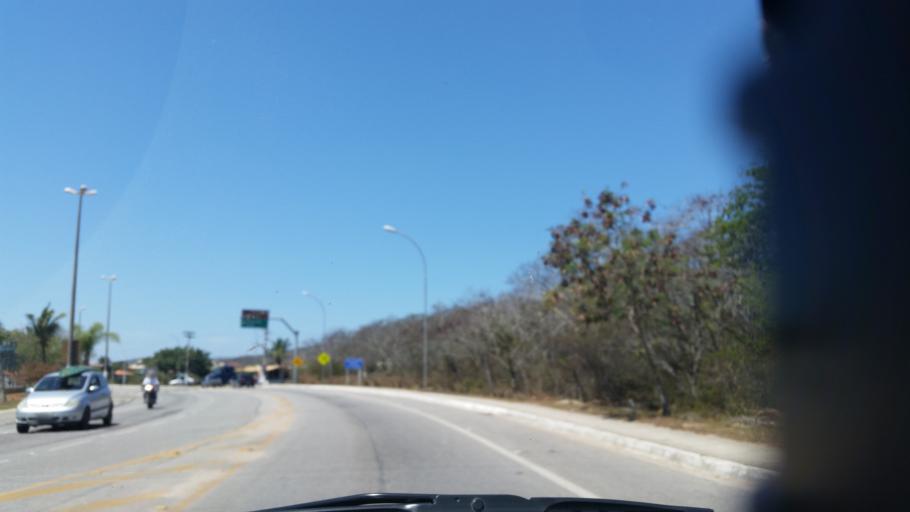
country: BR
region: Rio de Janeiro
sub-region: Armacao De Buzios
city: Armacao de Buzios
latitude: -22.7823
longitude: -41.9426
